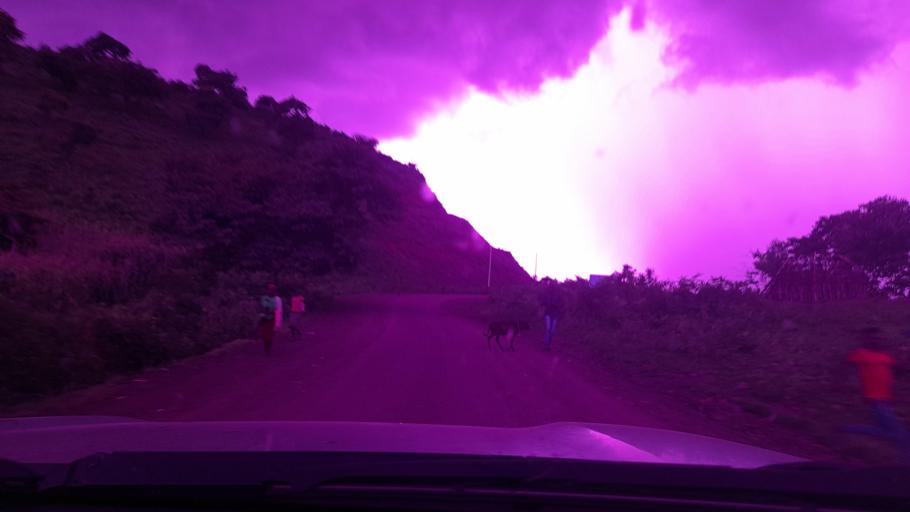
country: ET
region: Southern Nations, Nationalities, and People's Region
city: Mizan Teferi
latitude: 6.7389
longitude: 35.8652
